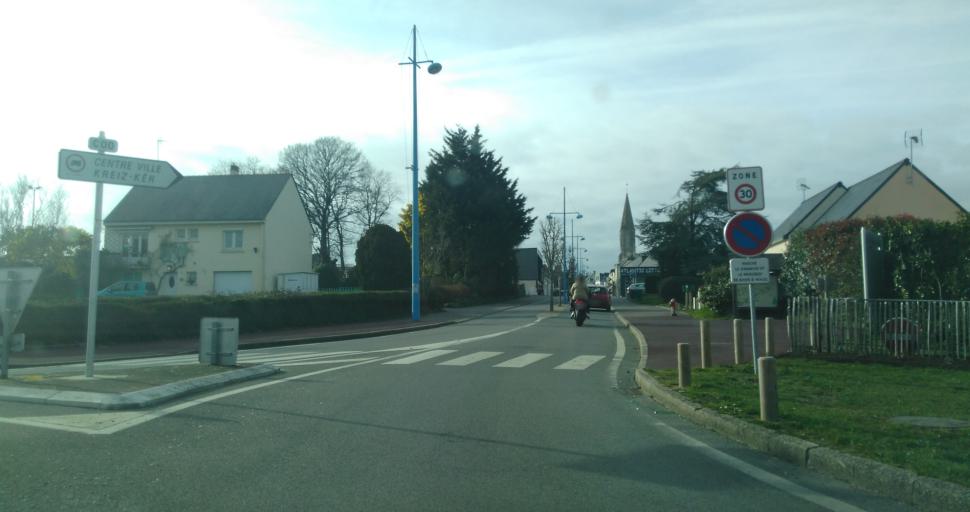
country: FR
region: Brittany
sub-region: Departement du Morbihan
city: Penestin
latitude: 47.4828
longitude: -2.4693
